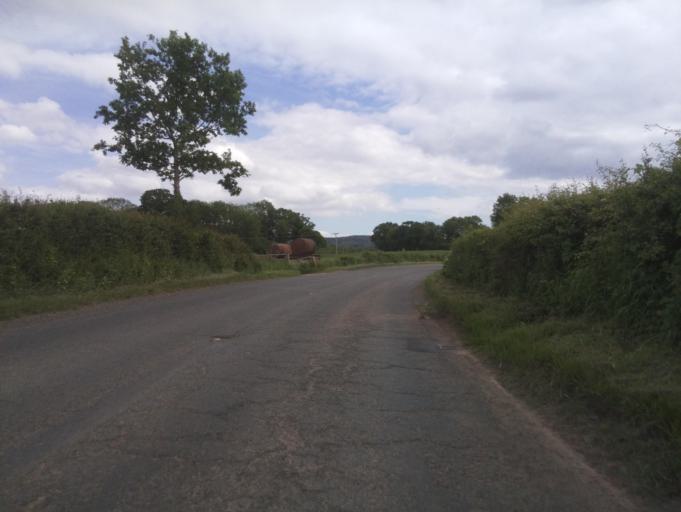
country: GB
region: England
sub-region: Herefordshire
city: Ledbury
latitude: 52.0741
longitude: -2.4526
